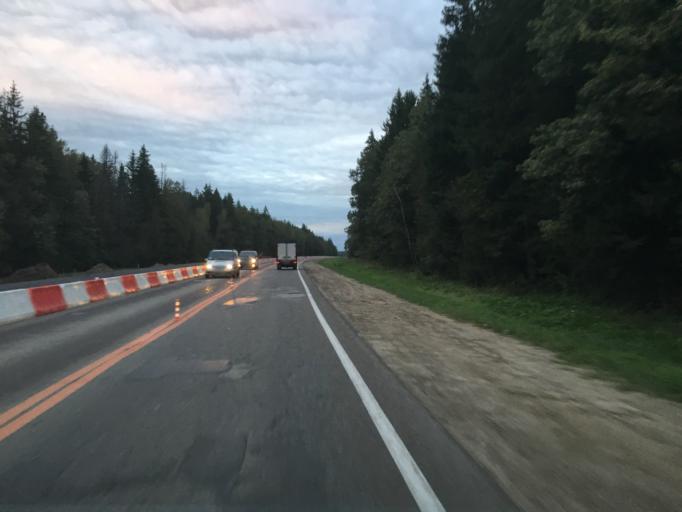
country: RU
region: Kaluga
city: Detchino
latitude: 54.6890
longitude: 36.2972
